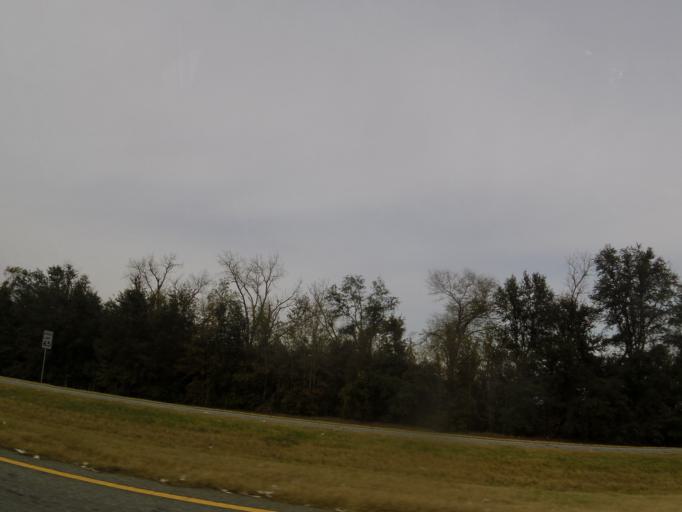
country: US
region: Georgia
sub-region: Seminole County
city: Donalsonville
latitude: 31.0093
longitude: -84.8081
